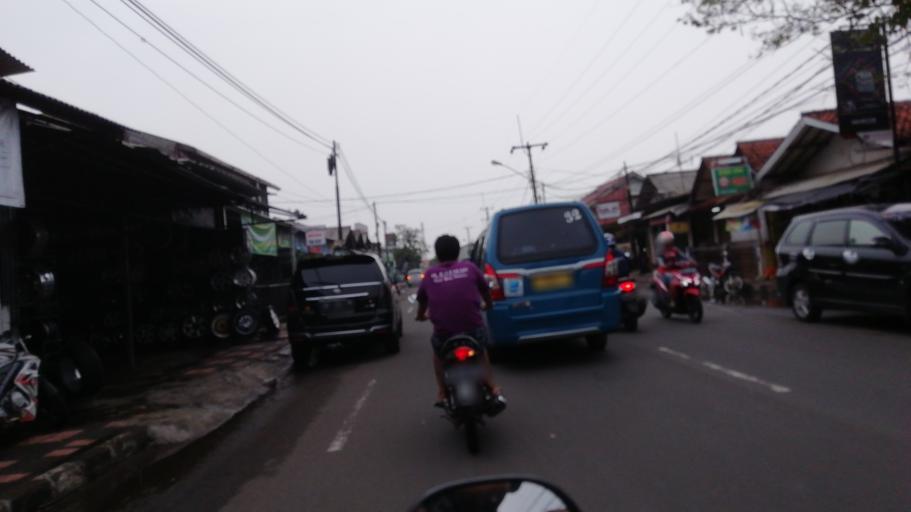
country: ID
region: West Java
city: Cibinong
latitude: -6.4982
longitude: 106.8109
